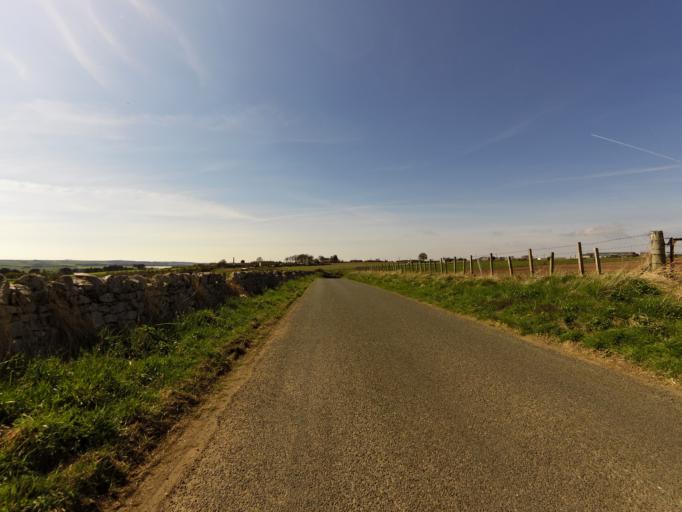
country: GB
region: Scotland
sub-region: Angus
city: Montrose
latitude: 56.6678
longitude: -2.5033
